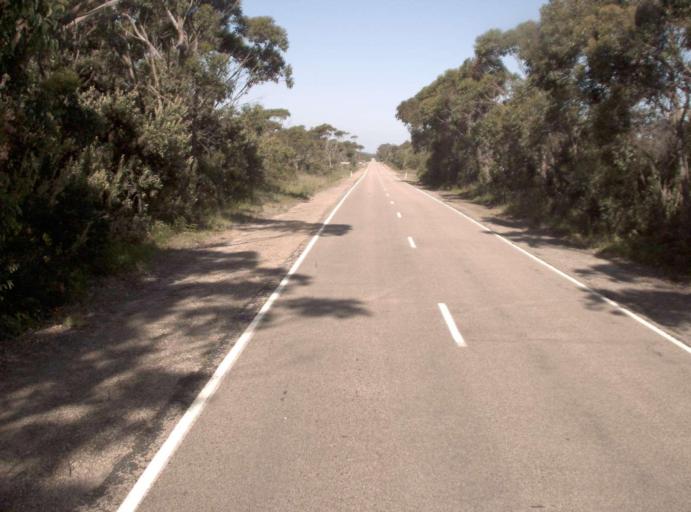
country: AU
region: Victoria
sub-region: East Gippsland
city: Lakes Entrance
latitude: -37.8020
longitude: 148.6325
